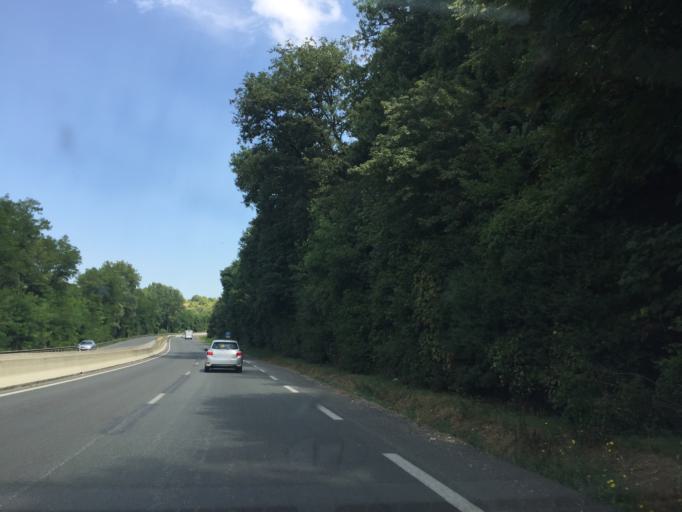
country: FR
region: Poitou-Charentes
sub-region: Departement de la Vienne
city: Biard
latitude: 46.5679
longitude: 0.3084
